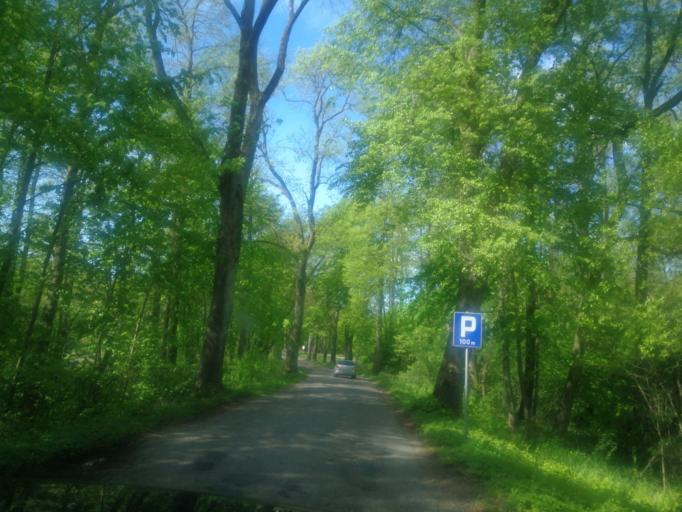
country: PL
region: Warmian-Masurian Voivodeship
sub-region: Powiat ilawski
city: Zalewo
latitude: 53.7511
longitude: 19.6924
